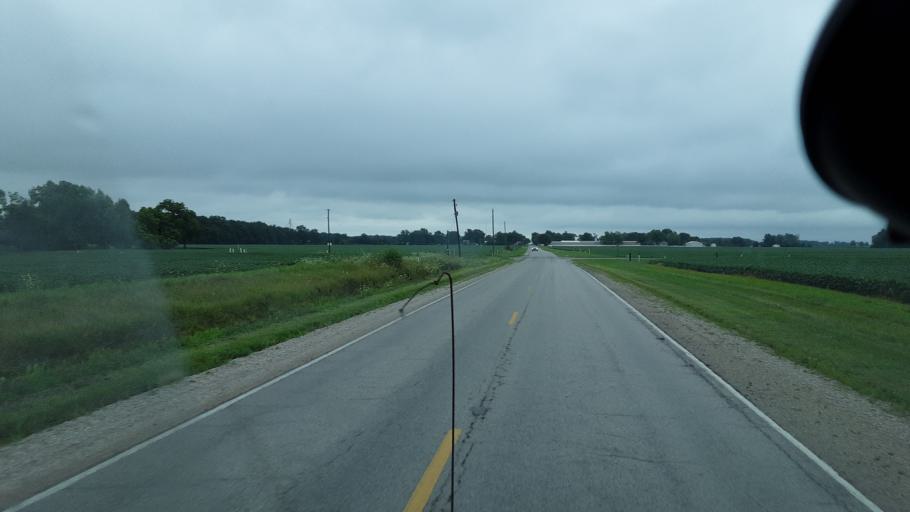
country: US
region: Indiana
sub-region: Wells County
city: Bluffton
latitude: 40.7876
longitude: -85.0909
